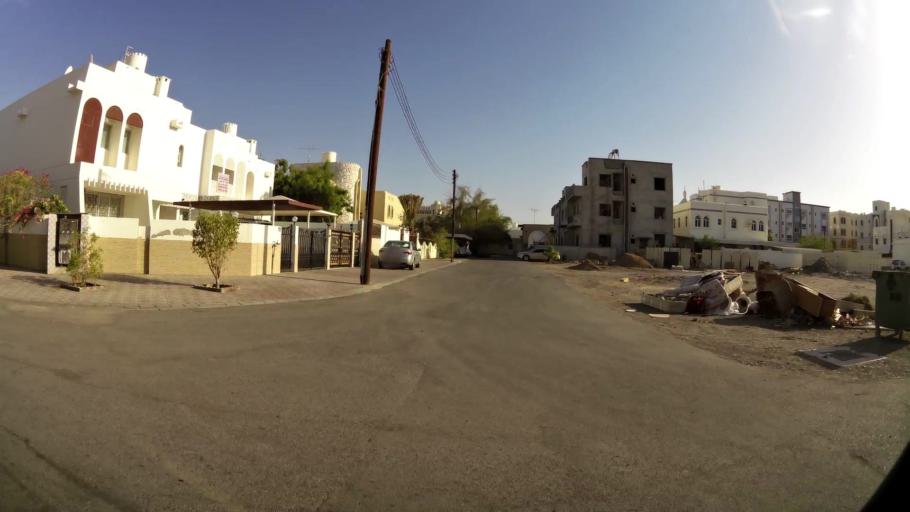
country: OM
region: Muhafazat Masqat
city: As Sib al Jadidah
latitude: 23.6364
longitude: 58.2029
